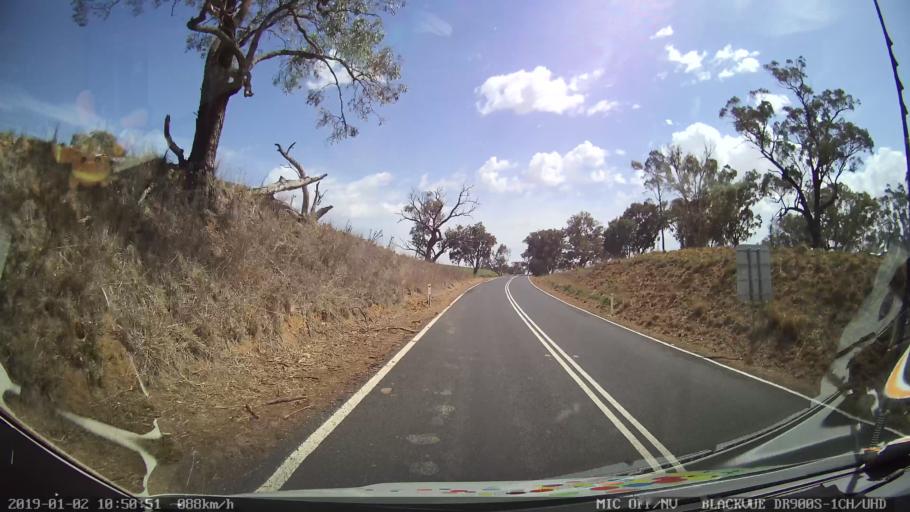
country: AU
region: New South Wales
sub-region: Cootamundra
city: Cootamundra
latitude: -34.7083
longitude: 148.2755
